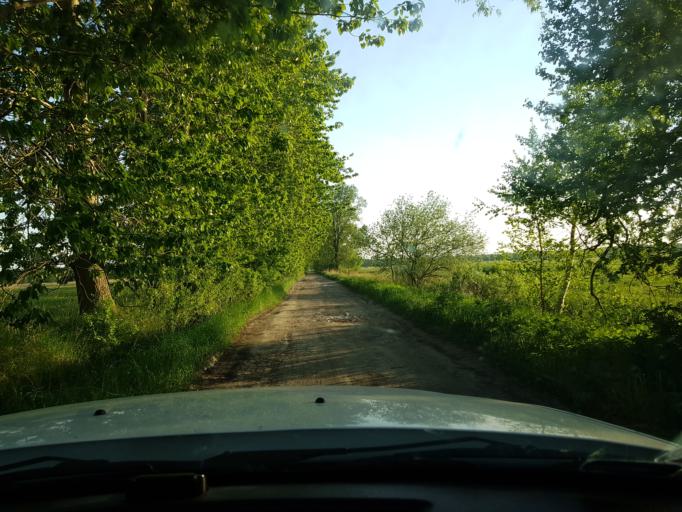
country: PL
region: West Pomeranian Voivodeship
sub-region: Powiat stargardzki
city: Kobylanka
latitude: 53.4070
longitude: 14.8934
